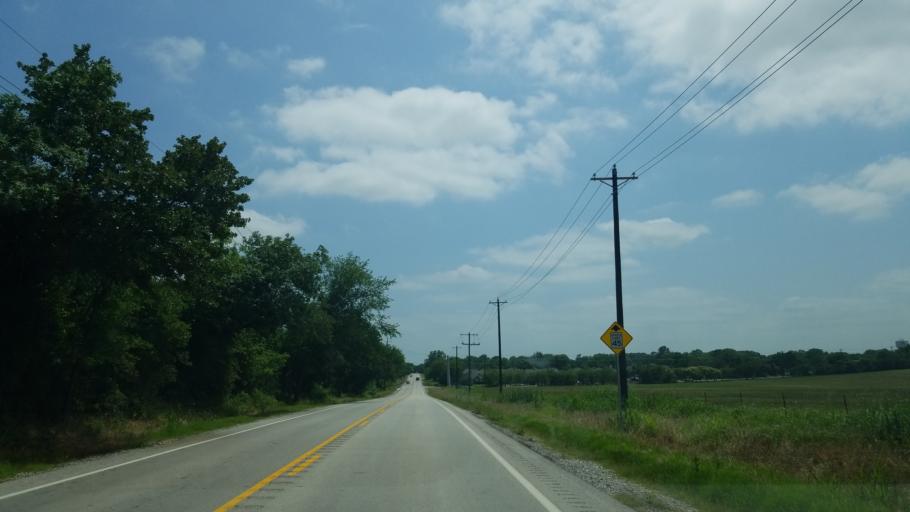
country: US
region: Texas
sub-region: Denton County
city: Aubrey
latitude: 33.3137
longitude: -96.9786
